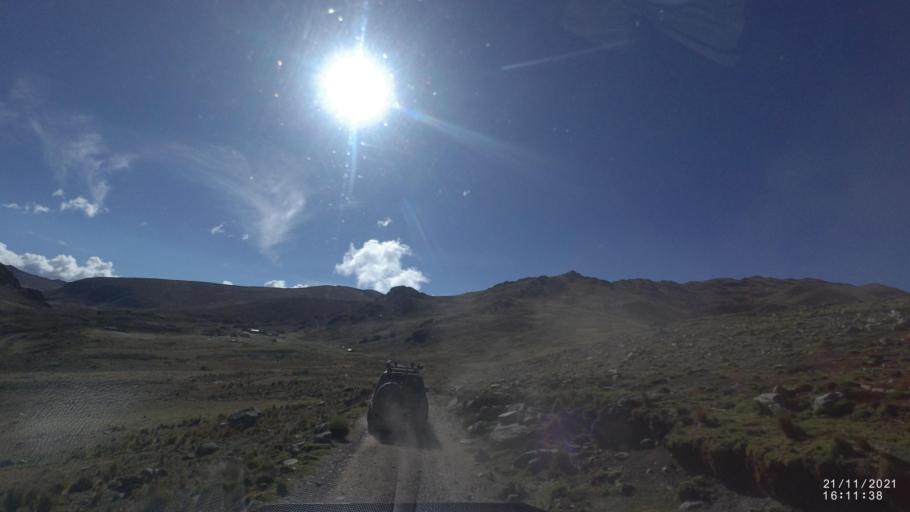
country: BO
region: Cochabamba
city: Cochabamba
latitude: -16.9956
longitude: -66.2717
